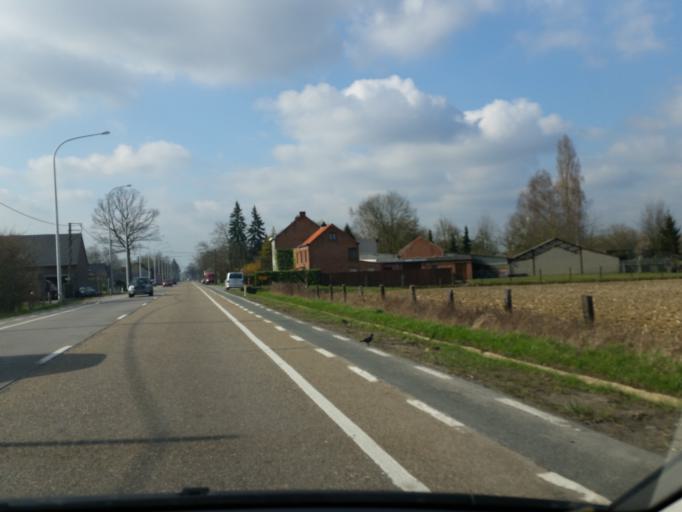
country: BE
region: Flanders
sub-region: Provincie Vlaams-Brabant
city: Herent
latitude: 50.9203
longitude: 4.6482
